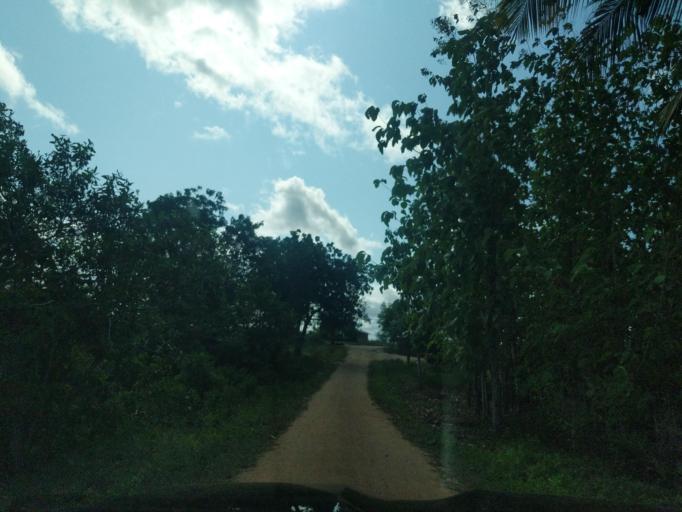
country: TZ
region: Tanga
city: Muheza
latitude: -5.4194
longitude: 38.6439
